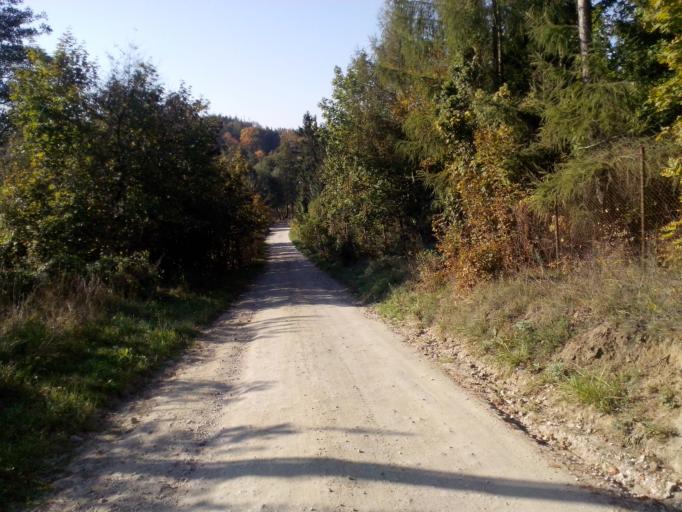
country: PL
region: Kujawsko-Pomorskie
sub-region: Powiat brodnicki
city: Gorzno
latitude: 53.1980
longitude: 19.6593
